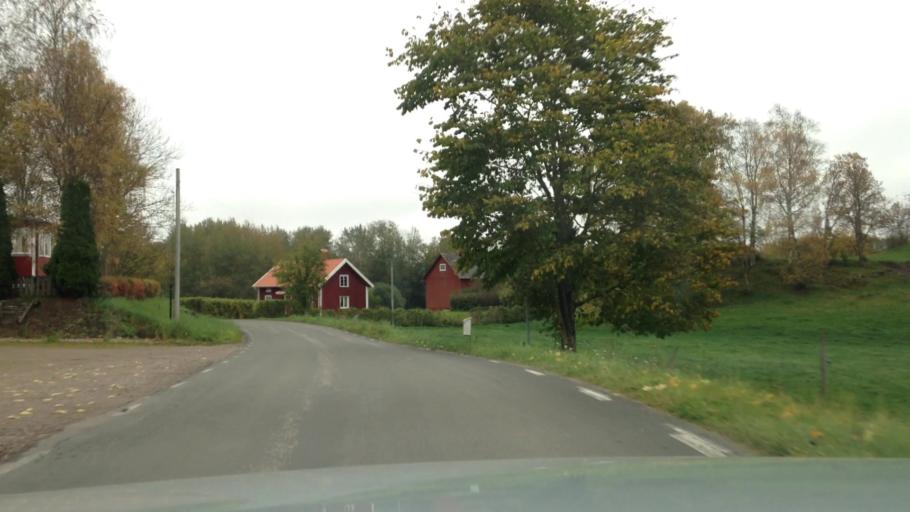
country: SE
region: Vaestra Goetaland
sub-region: Falkopings Kommun
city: Akarp
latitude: 58.2705
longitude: 13.7005
